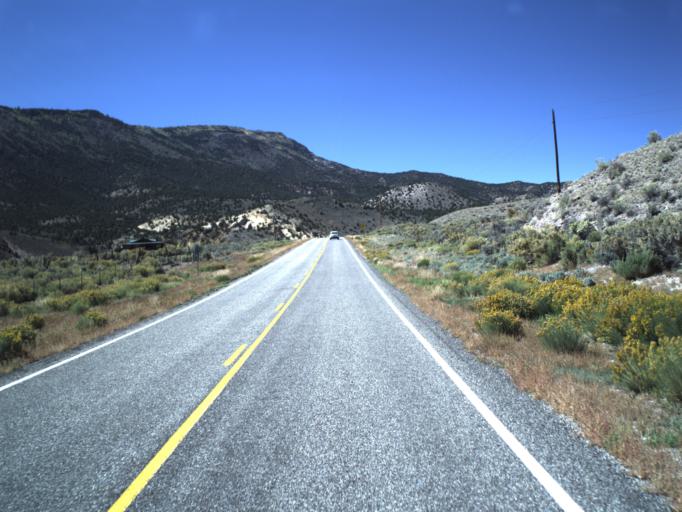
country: US
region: Utah
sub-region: Piute County
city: Junction
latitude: 38.1688
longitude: -112.0492
